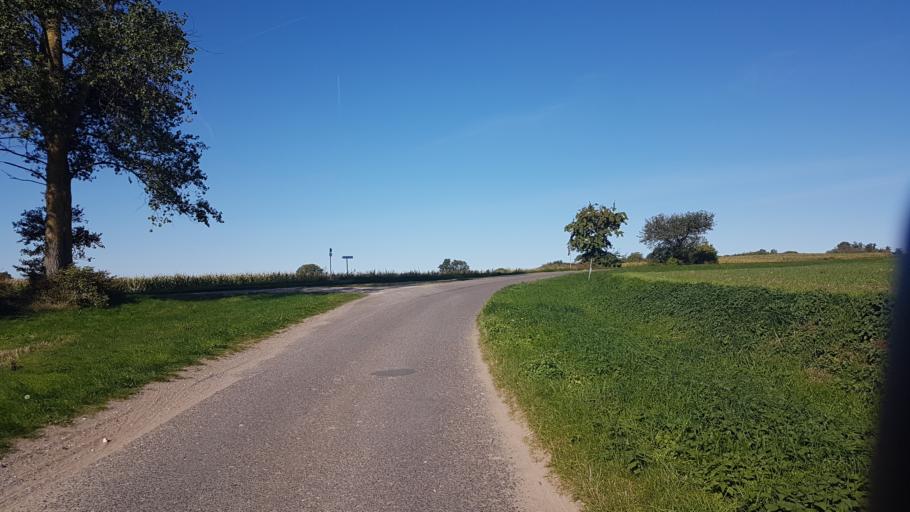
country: DE
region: Mecklenburg-Vorpommern
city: Sagard
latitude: 54.5332
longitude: 13.5130
